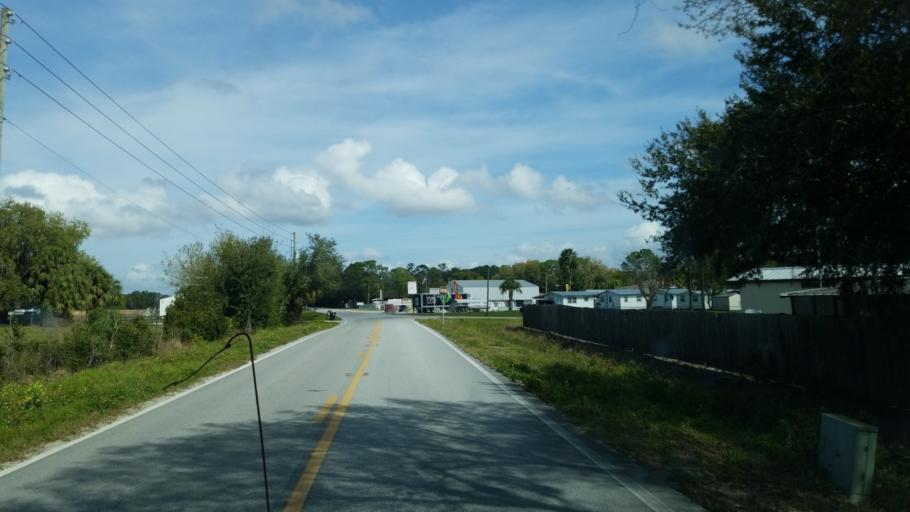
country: US
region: Florida
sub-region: Polk County
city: Babson Park
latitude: 27.9432
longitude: -81.4258
